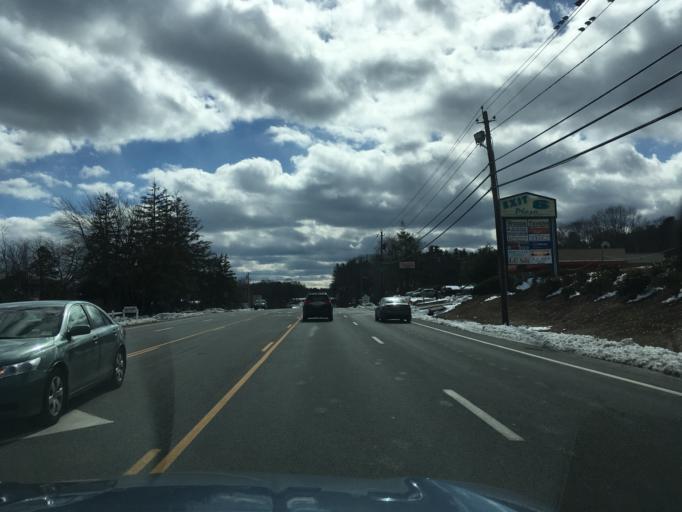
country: US
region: Rhode Island
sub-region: Kent County
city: West Greenwich
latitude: 41.6571
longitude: -71.6041
